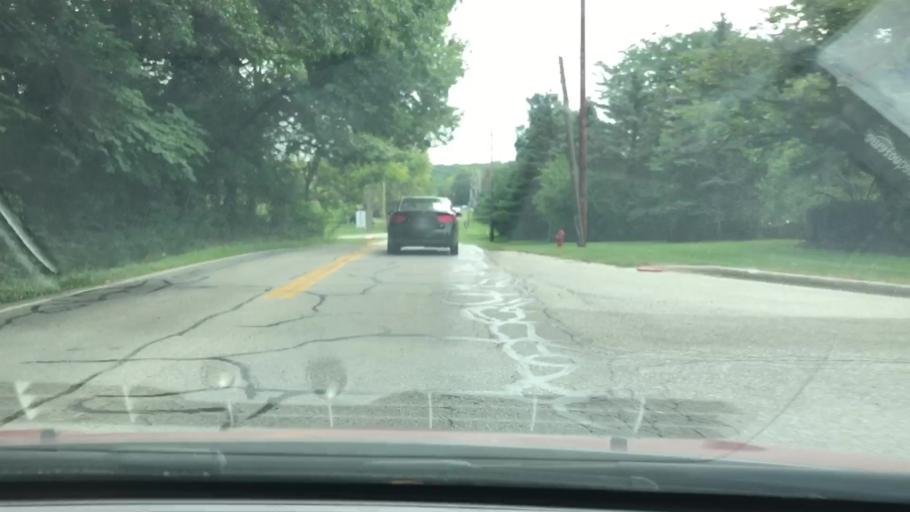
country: US
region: Ohio
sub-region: Franklin County
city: Huber Ridge
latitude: 40.0943
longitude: -82.8961
